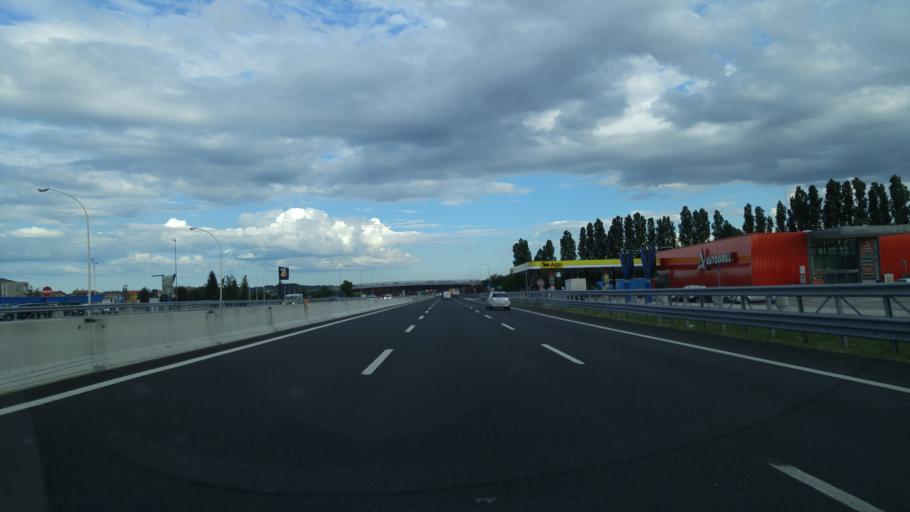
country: IT
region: Emilia-Romagna
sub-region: Provincia di Rimini
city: Coriano
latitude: 43.9951
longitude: 12.6183
